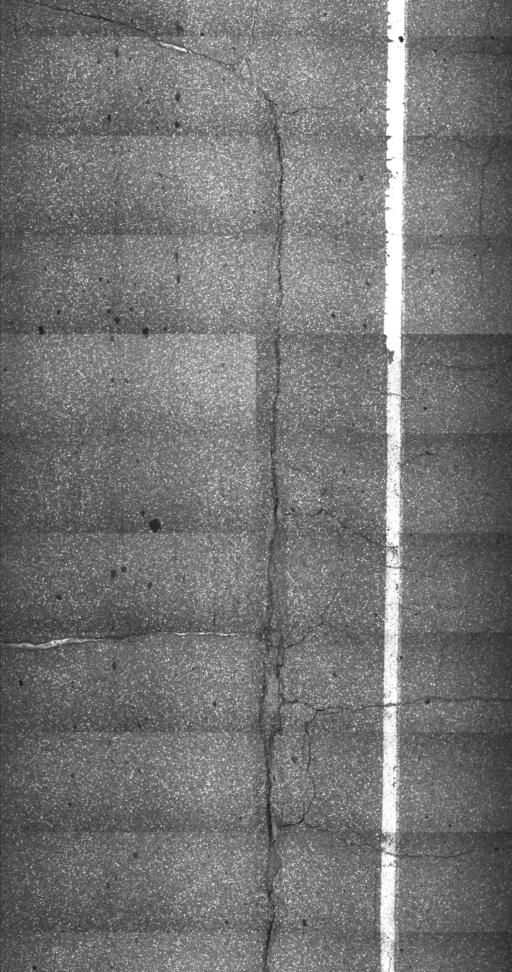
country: US
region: Vermont
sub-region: Windsor County
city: Windsor
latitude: 43.4908
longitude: -72.3861
